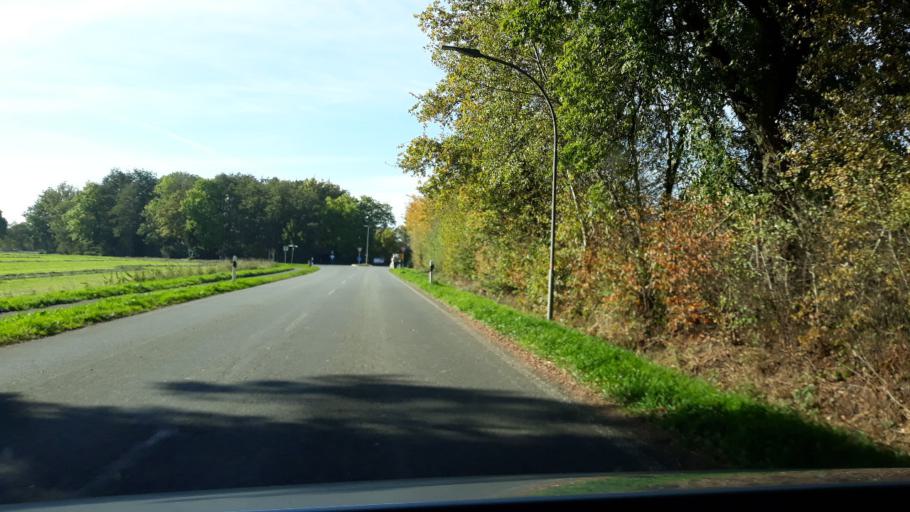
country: DE
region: Schleswig-Holstein
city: Borm
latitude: 54.4109
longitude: 9.3811
